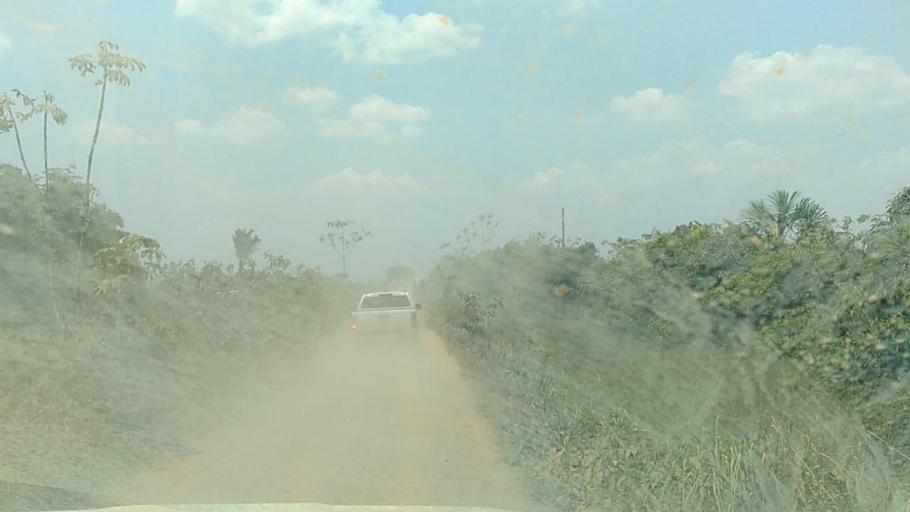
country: BR
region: Rondonia
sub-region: Porto Velho
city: Porto Velho
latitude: -8.7291
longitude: -63.2959
